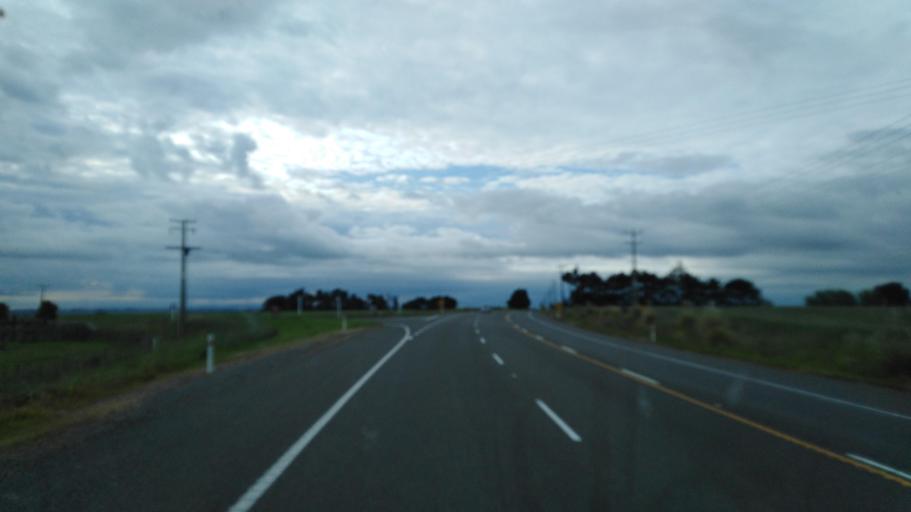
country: NZ
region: Manawatu-Wanganui
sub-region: Rangitikei District
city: Bulls
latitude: -40.1335
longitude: 175.3624
